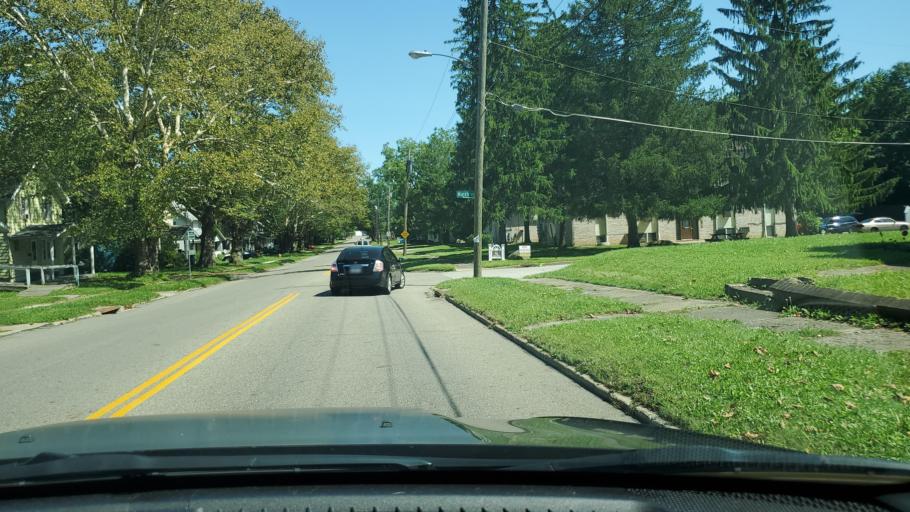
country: US
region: Ohio
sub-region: Mahoning County
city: Struthers
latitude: 41.0606
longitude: -80.6106
